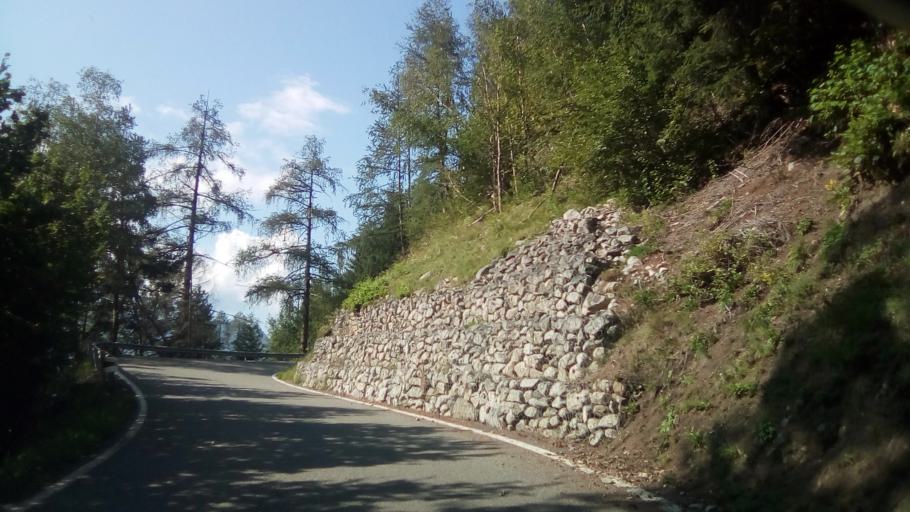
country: CH
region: Valais
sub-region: Martigny District
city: Martigny-Combe
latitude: 46.0640
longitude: 7.0763
